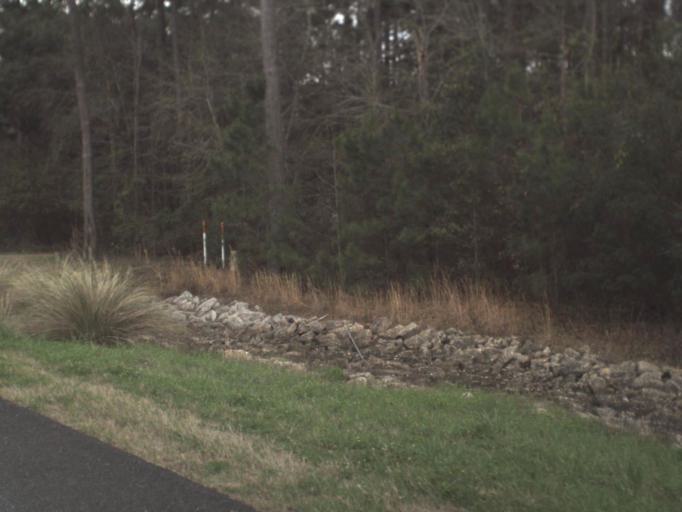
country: US
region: Florida
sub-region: Leon County
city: Tallahassee
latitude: 30.5726
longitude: -84.2061
